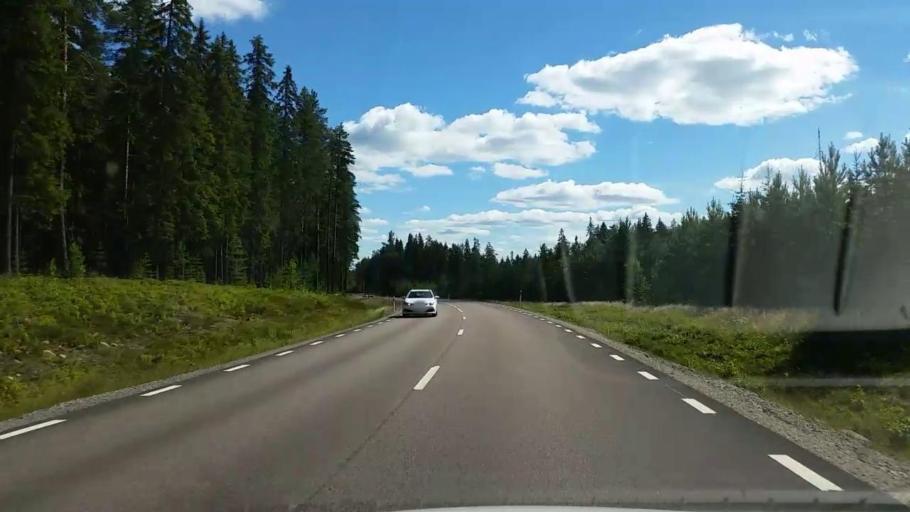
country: SE
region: Dalarna
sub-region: Faluns Kommun
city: Svardsjo
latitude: 60.7615
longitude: 15.7537
